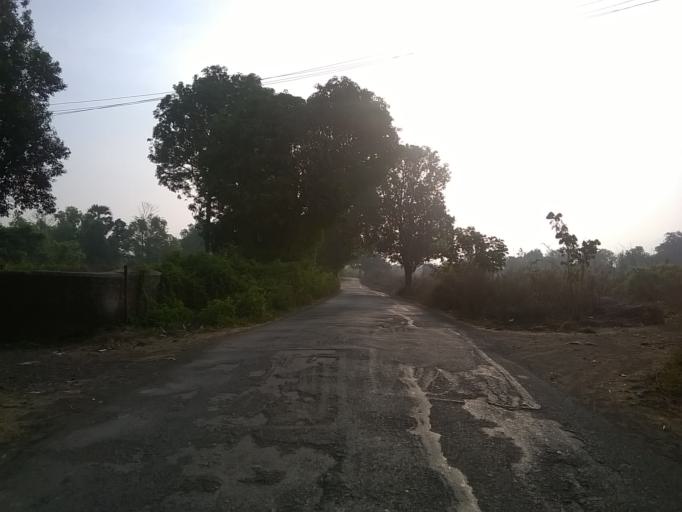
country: IN
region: Maharashtra
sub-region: Raigarh
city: Kalundri
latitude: 19.0154
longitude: 73.1764
